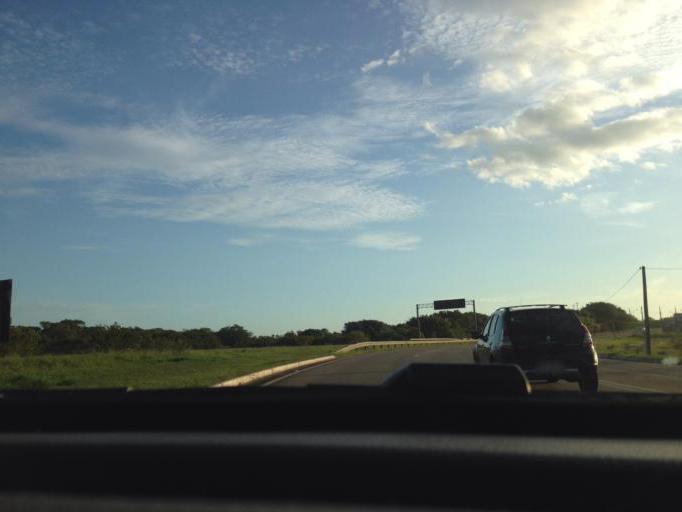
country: BR
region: Espirito Santo
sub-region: Guarapari
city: Guarapari
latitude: -20.6223
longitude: -40.4339
